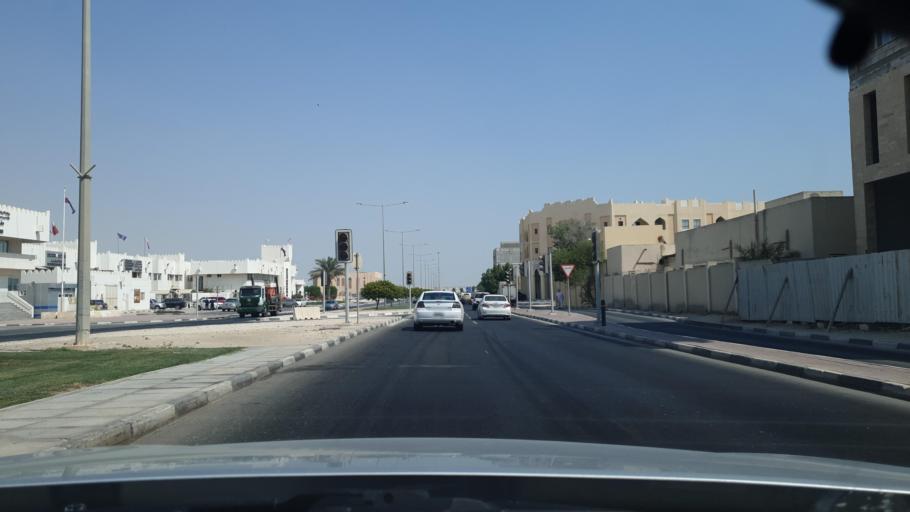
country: QA
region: Al Khawr
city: Al Khawr
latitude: 25.6879
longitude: 51.4963
